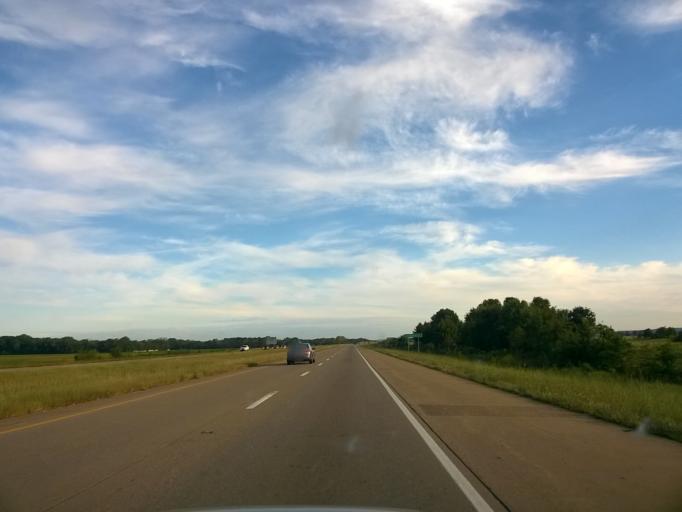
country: US
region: Indiana
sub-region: Vanderburgh County
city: Melody Hill
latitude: 38.0360
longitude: -87.4731
